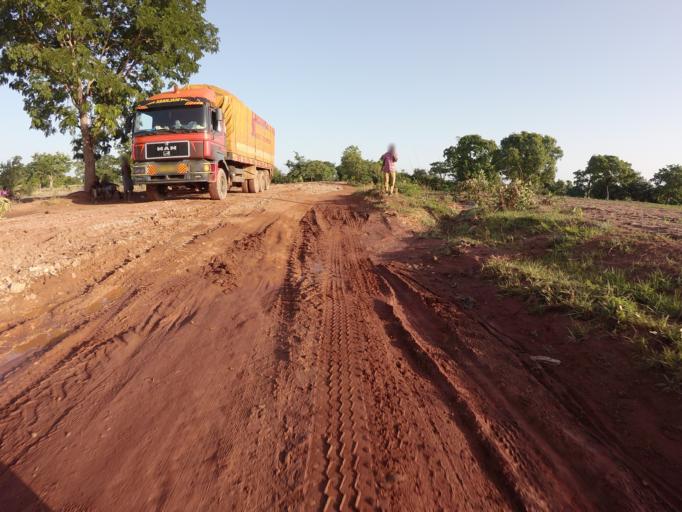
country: TG
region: Savanes
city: Sansanne-Mango
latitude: 10.3484
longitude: -0.0928
